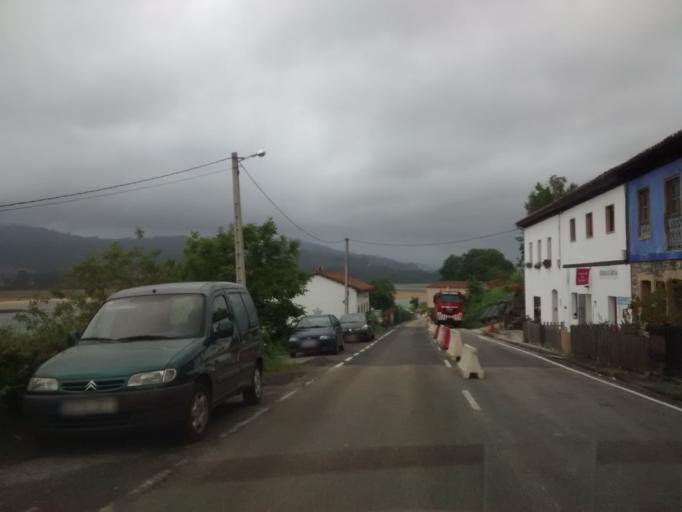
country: ES
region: Asturias
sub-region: Province of Asturias
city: Villaviciosa
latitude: 43.5261
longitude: -5.3915
